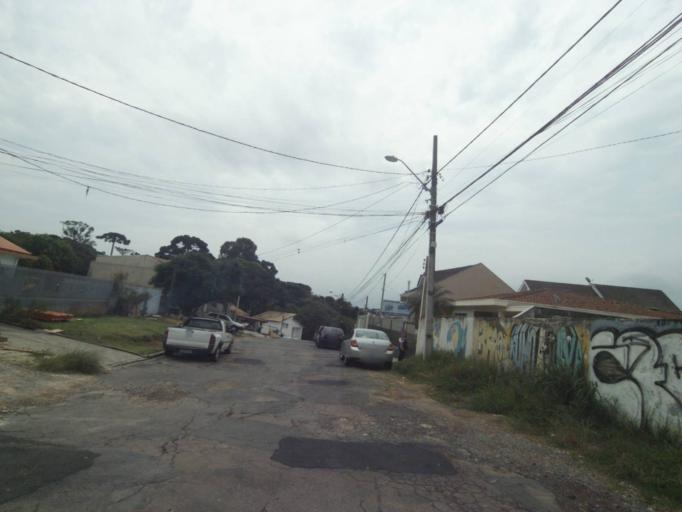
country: BR
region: Parana
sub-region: Curitiba
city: Curitiba
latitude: -25.4148
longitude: -49.2967
